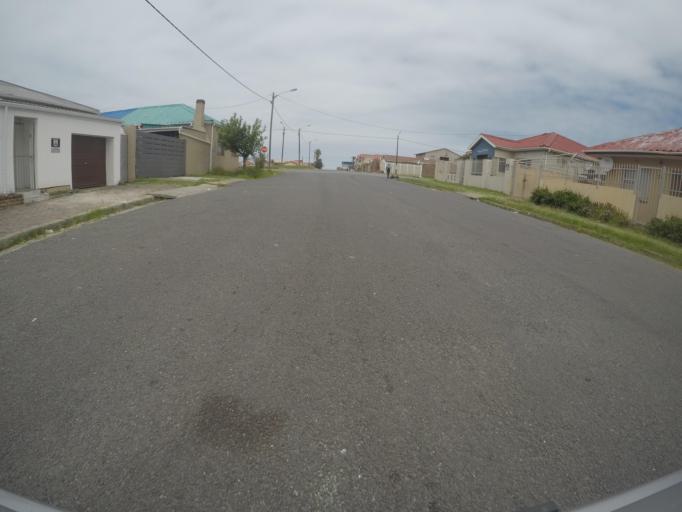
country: ZA
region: Eastern Cape
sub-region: Buffalo City Metropolitan Municipality
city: East London
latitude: -33.0138
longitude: 27.9138
